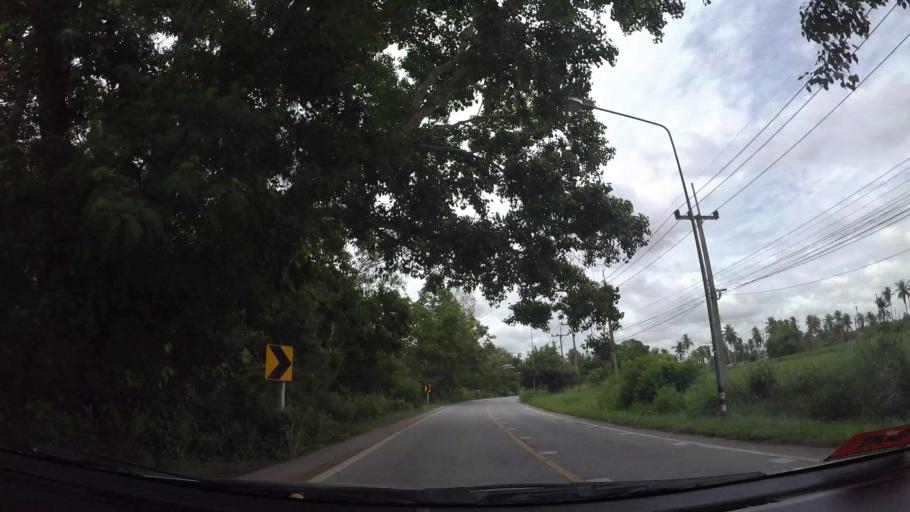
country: TH
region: Chon Buri
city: Si Racha
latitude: 13.1873
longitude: 100.9802
